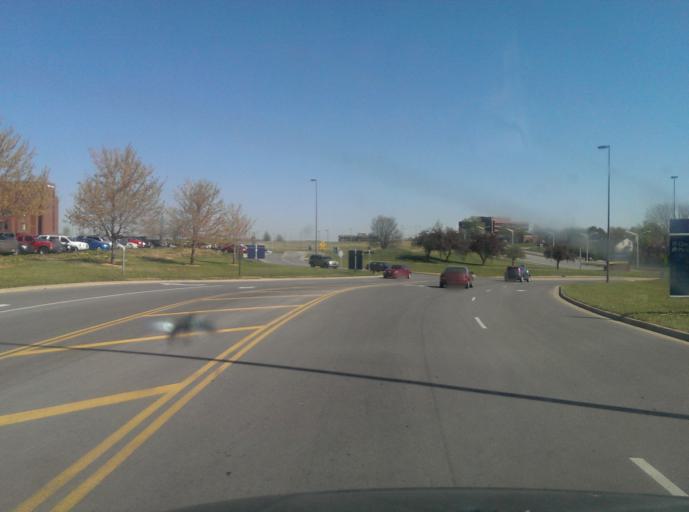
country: US
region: Kansas
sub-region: Johnson County
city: Lenexa
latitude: 38.9220
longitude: -94.7249
